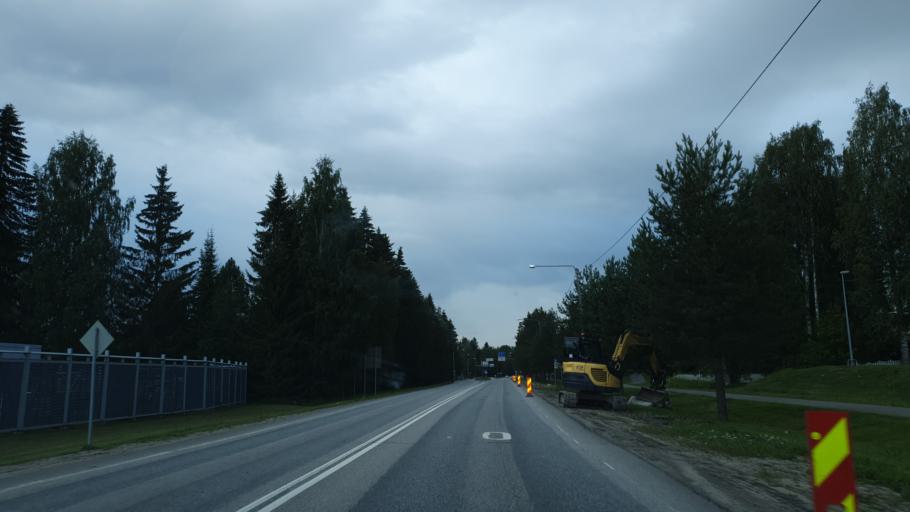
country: FI
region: North Karelia
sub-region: Pielisen Karjala
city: Lieksa
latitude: 63.3171
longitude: 30.0233
